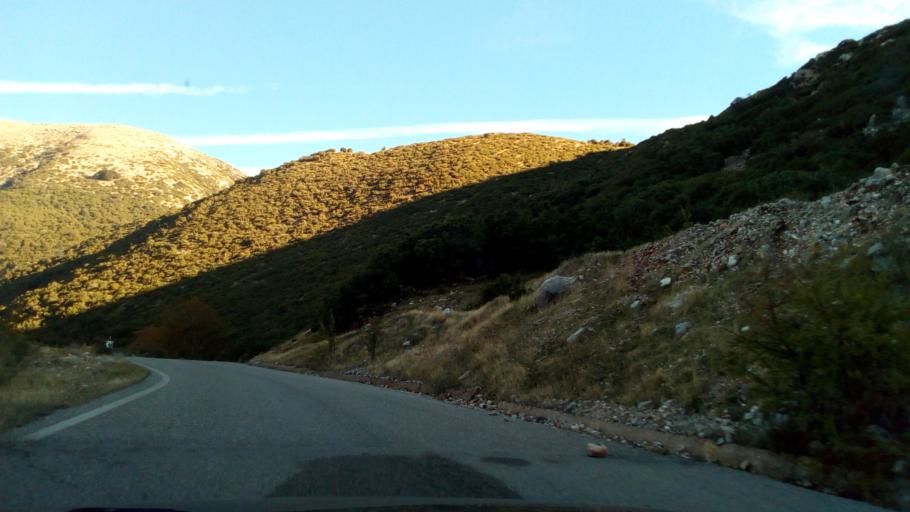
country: GR
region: West Greece
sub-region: Nomos Aitolias kai Akarnanias
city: Nafpaktos
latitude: 38.4897
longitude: 21.8577
